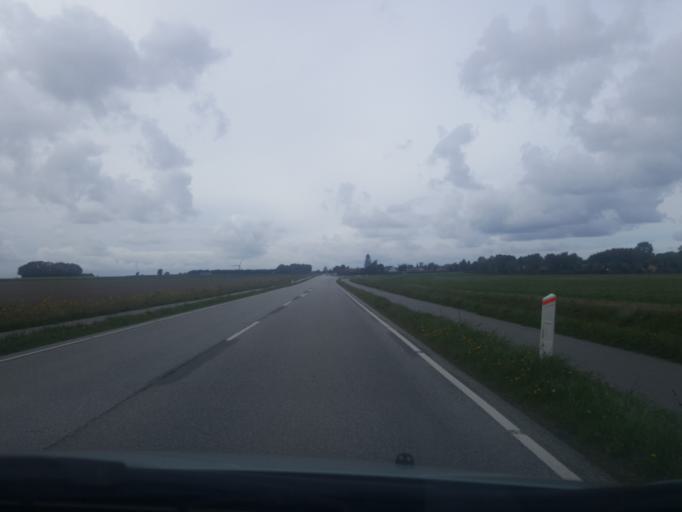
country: DK
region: Zealand
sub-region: Guldborgsund Kommune
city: Nykobing Falster
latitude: 54.7025
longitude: 11.9296
